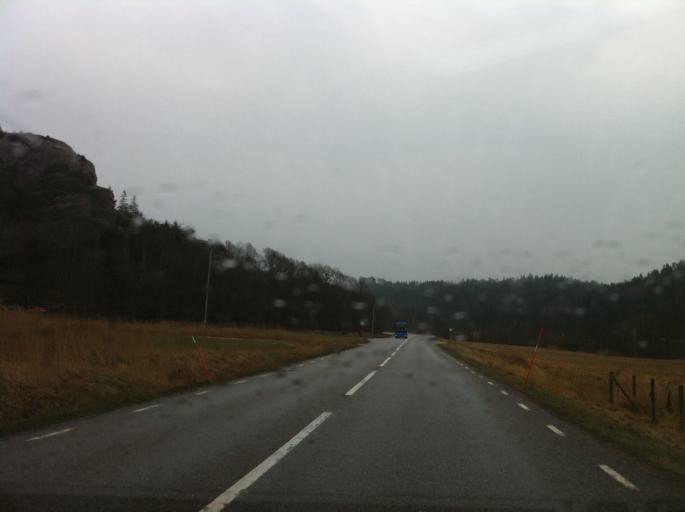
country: SE
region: Vaestra Goetaland
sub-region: Lysekils Kommun
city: Brastad
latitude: 58.4567
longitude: 11.4653
